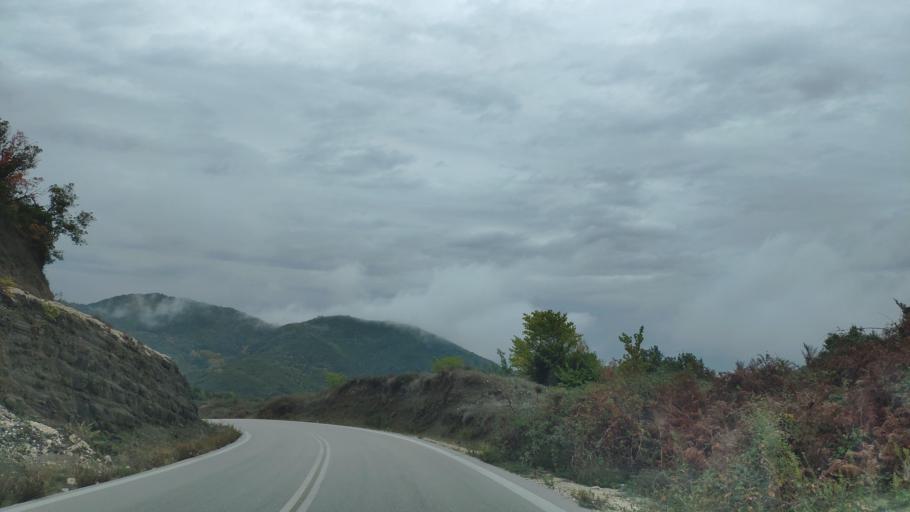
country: GR
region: Epirus
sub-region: Nomos Thesprotias
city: Paramythia
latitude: 39.4834
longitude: 20.6733
